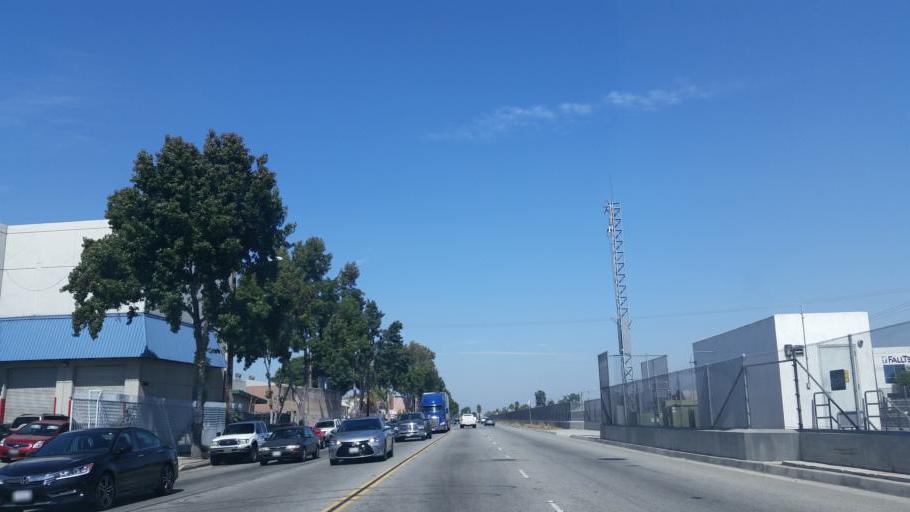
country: US
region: California
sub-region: Los Angeles County
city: Compton
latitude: 33.8827
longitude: -118.2183
